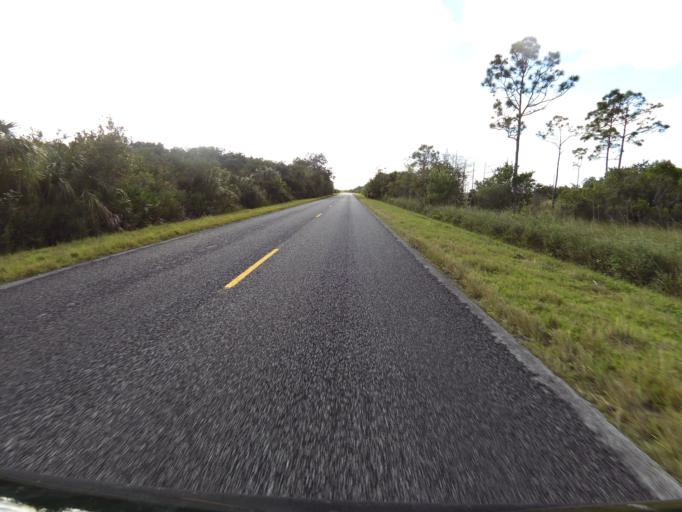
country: US
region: Florida
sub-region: Miami-Dade County
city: Florida City
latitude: 25.3943
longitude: -80.7992
